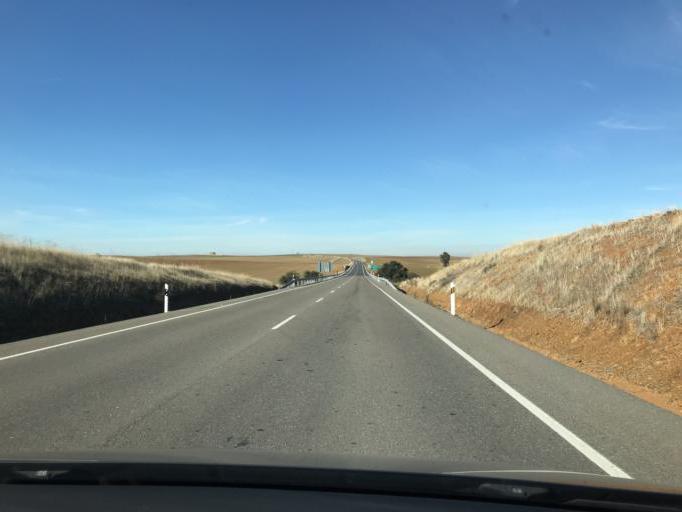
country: ES
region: Extremadura
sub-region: Provincia de Badajoz
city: Granja de Torrehermosa
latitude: 38.2939
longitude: -5.5427
